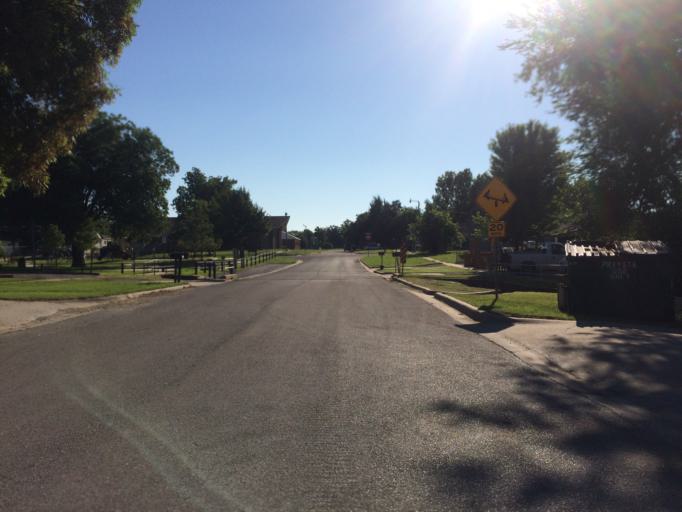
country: US
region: Oklahoma
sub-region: Cleveland County
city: Norman
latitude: 35.2222
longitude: -97.4348
